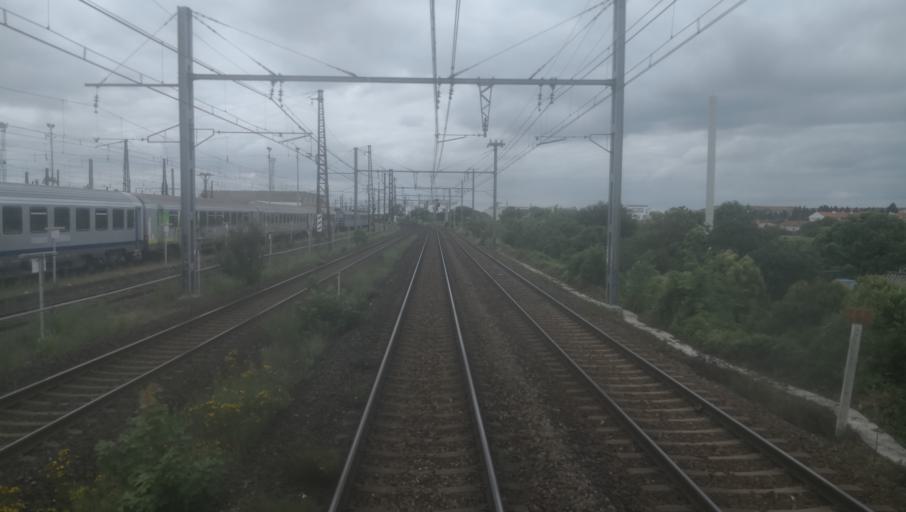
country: FR
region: Midi-Pyrenees
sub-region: Departement de la Haute-Garonne
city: Toulouse
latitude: 43.6232
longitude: 1.4488
